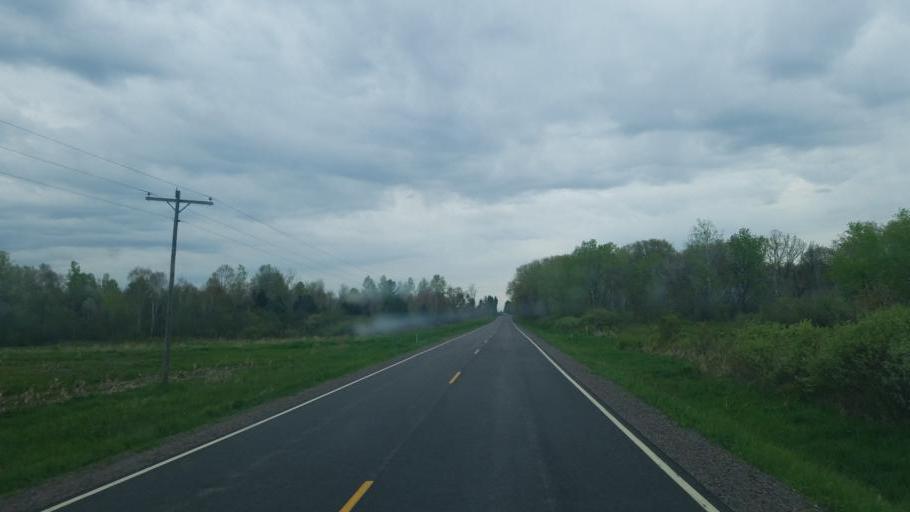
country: US
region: Wisconsin
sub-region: Wood County
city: Marshfield
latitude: 44.4889
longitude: -90.2796
